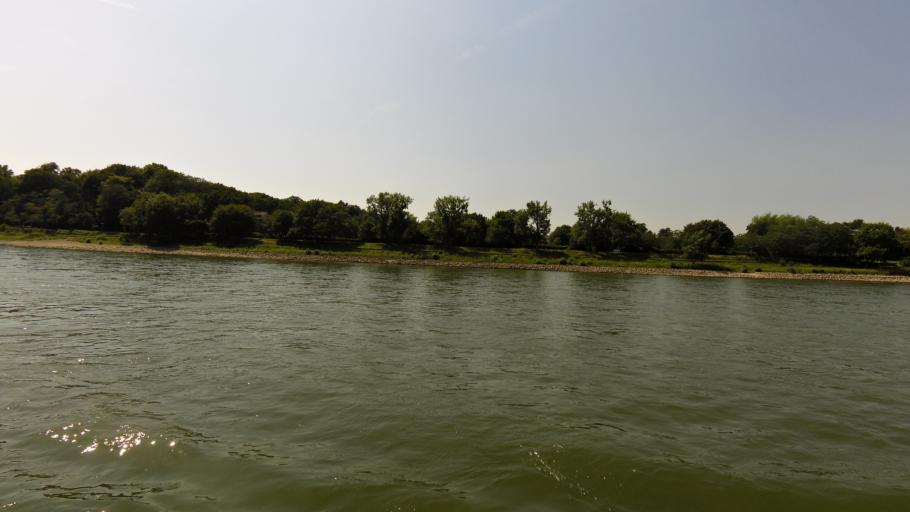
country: DE
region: North Rhine-Westphalia
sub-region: Regierungsbezirk Koln
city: Konigswinter
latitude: 50.6787
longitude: 7.1842
